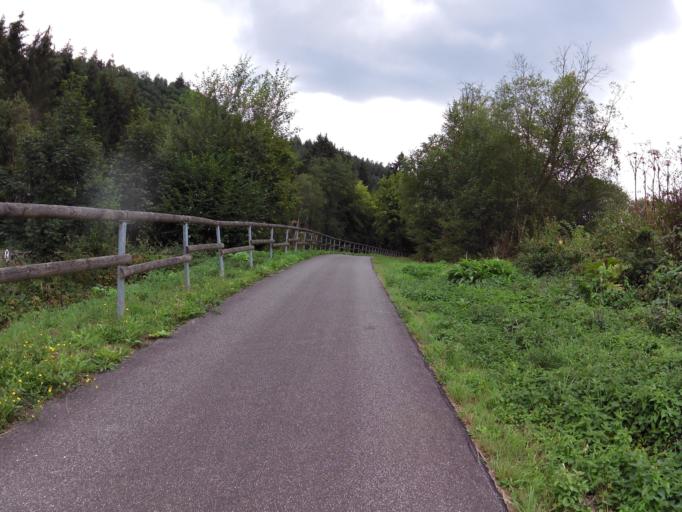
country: DE
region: Rheinland-Pfalz
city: Zendscheid
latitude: 50.0855
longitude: 6.6045
